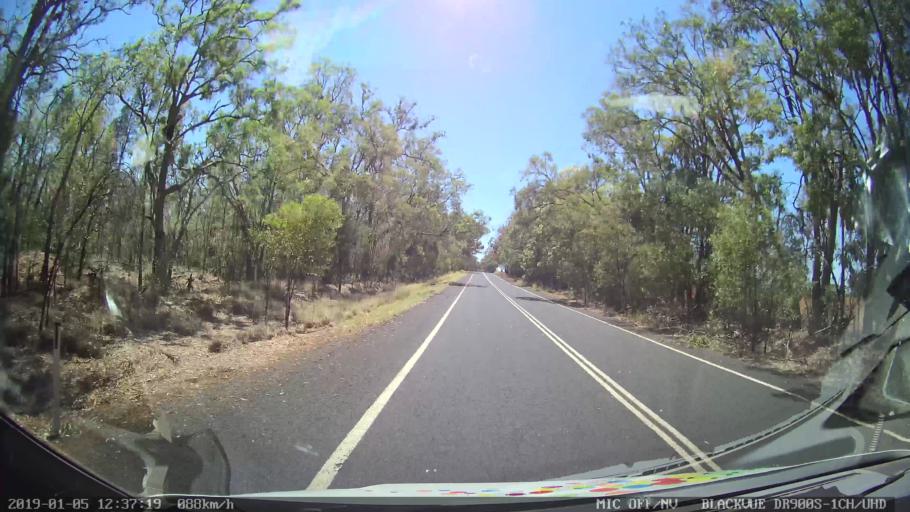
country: AU
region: New South Wales
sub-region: Warrumbungle Shire
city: Coonabarabran
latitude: -31.2038
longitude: 149.4530
